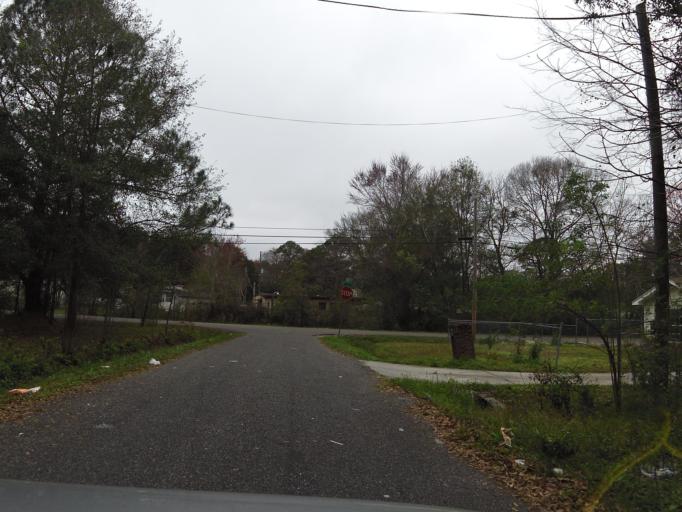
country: US
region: Florida
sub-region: Duval County
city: Jacksonville
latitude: 30.3748
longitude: -81.7010
